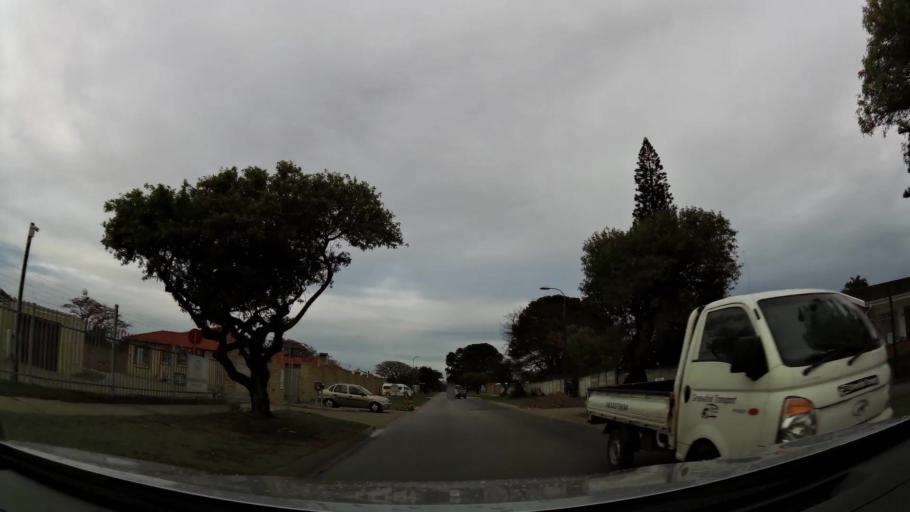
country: ZA
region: Eastern Cape
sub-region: Nelson Mandela Bay Metropolitan Municipality
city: Port Elizabeth
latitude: -33.9829
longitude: 25.5587
